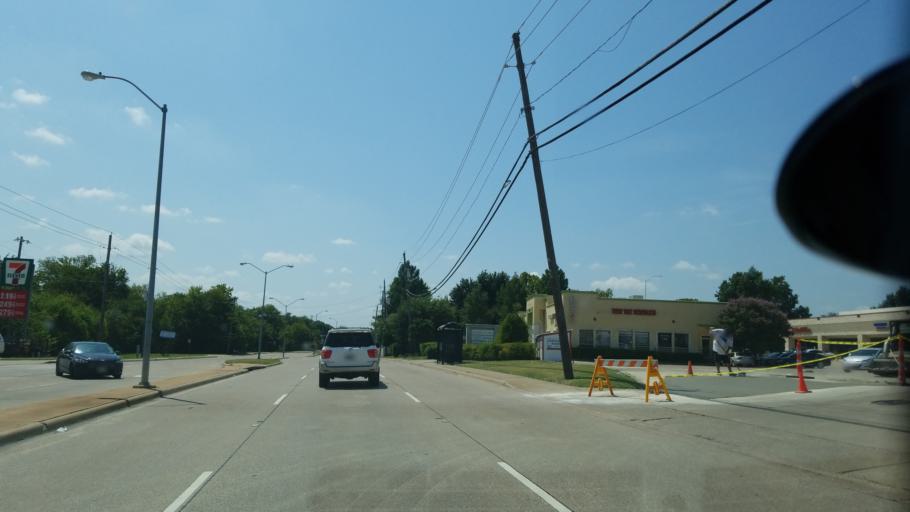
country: US
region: Texas
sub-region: Dallas County
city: Richardson
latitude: 32.9225
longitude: -96.7181
